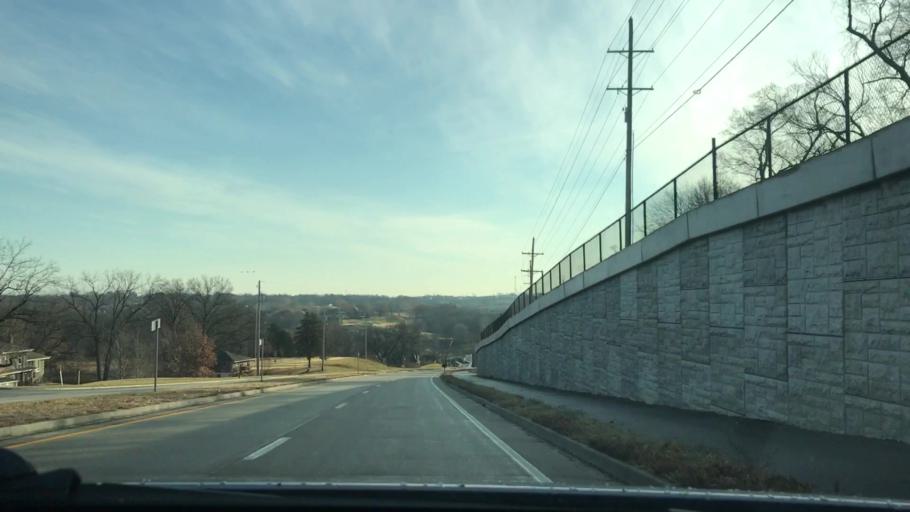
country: US
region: Missouri
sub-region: Platte County
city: Weatherby Lake
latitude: 39.2118
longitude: -94.7205
